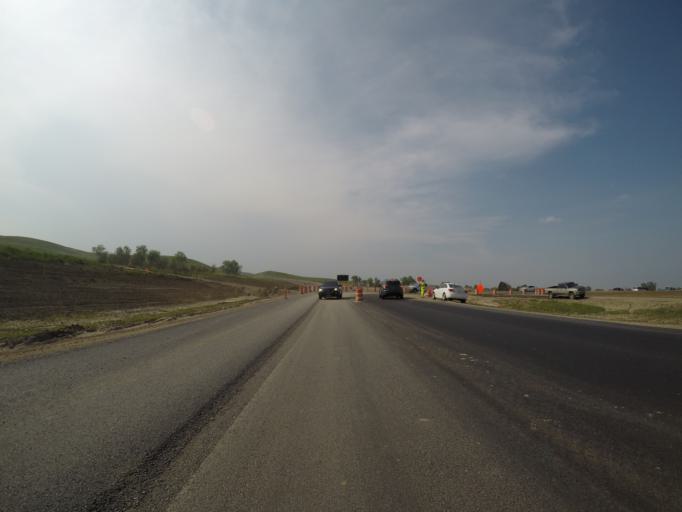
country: US
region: Montana
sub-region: Yellowstone County
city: Laurel
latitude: 45.5372
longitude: -108.8518
